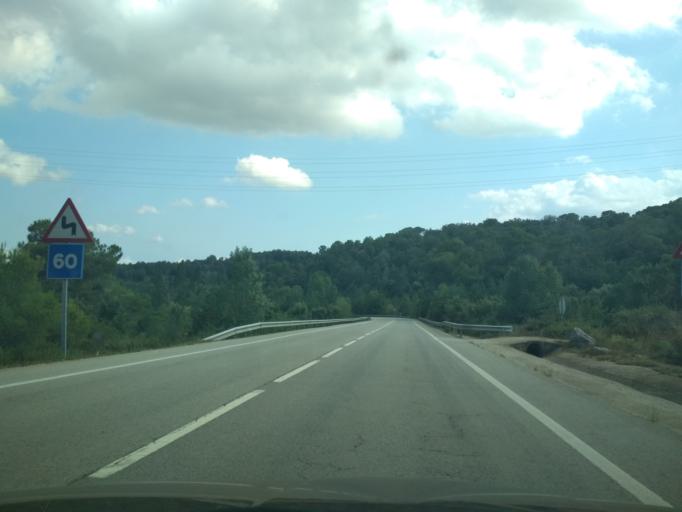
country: ES
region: Catalonia
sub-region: Provincia de Barcelona
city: Sant Feliu de Codines
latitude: 41.7119
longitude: 2.1539
